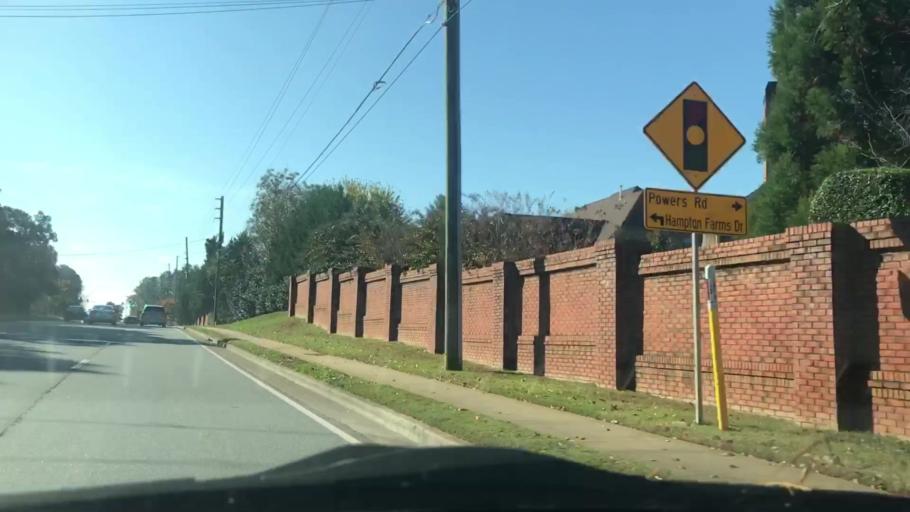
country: US
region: Georgia
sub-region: Fulton County
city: Sandy Springs
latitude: 33.9579
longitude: -84.4119
